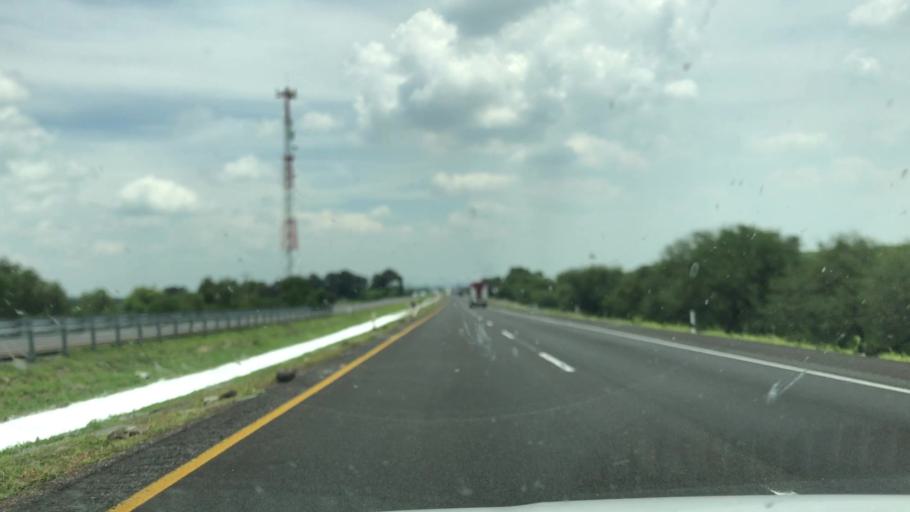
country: MX
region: Guanajuato
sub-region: Salamanca
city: San Vicente de Flores
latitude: 20.6198
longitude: -101.2333
